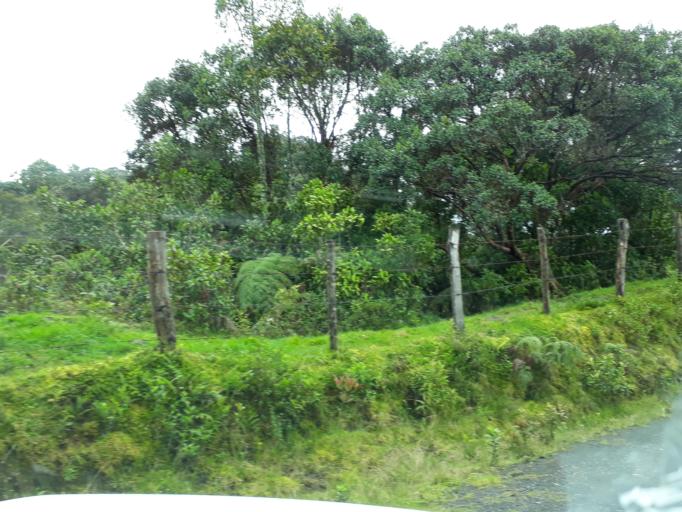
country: CO
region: Cundinamarca
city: Junin
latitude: 4.7286
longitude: -73.6269
